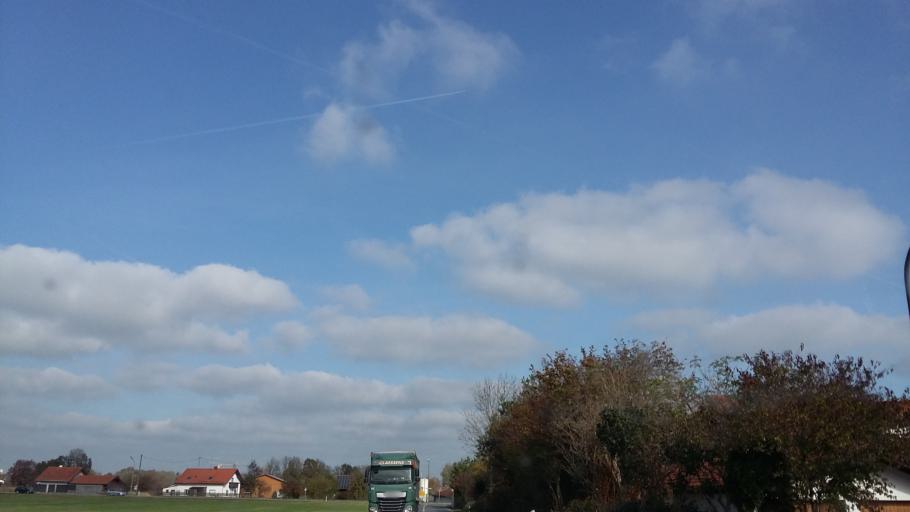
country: DE
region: Bavaria
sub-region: Upper Bavaria
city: Bruckmuhl
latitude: 47.8621
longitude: 11.9386
